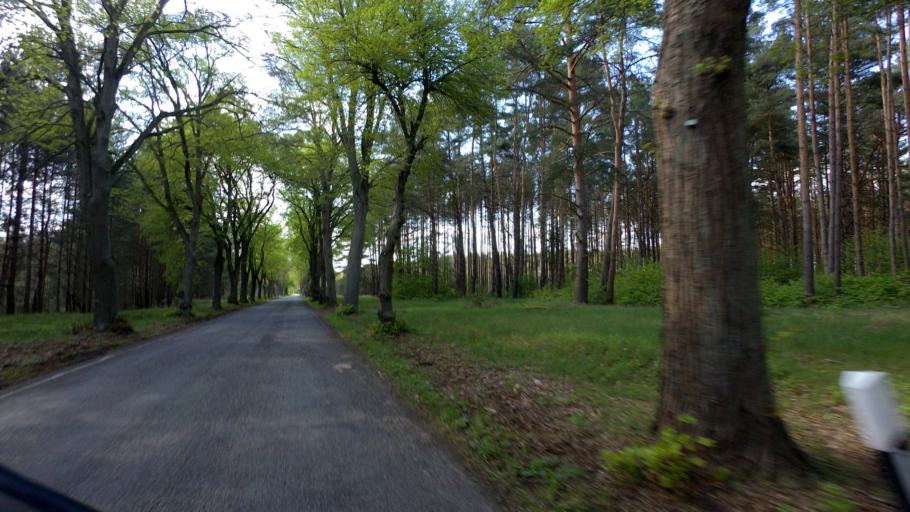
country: DE
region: Brandenburg
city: Templin
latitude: 52.9971
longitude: 13.5094
